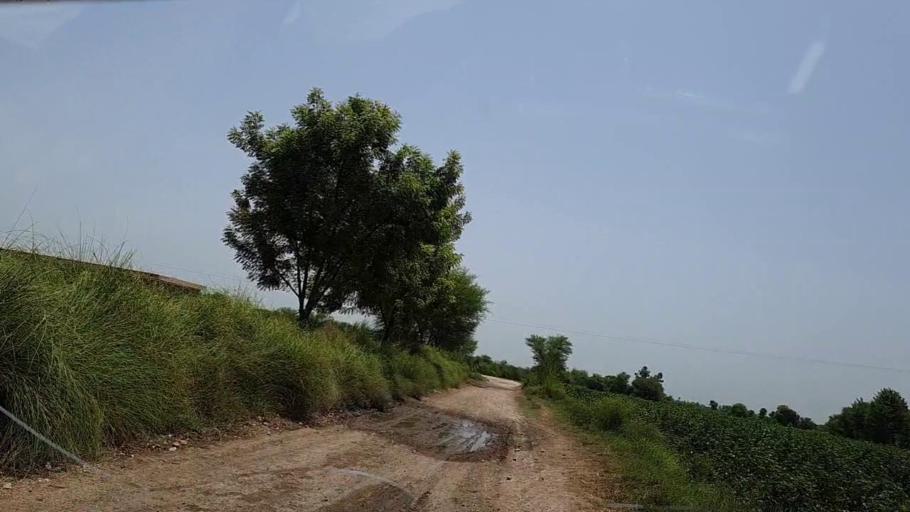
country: PK
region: Sindh
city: Tharu Shah
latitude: 26.9272
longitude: 68.0410
